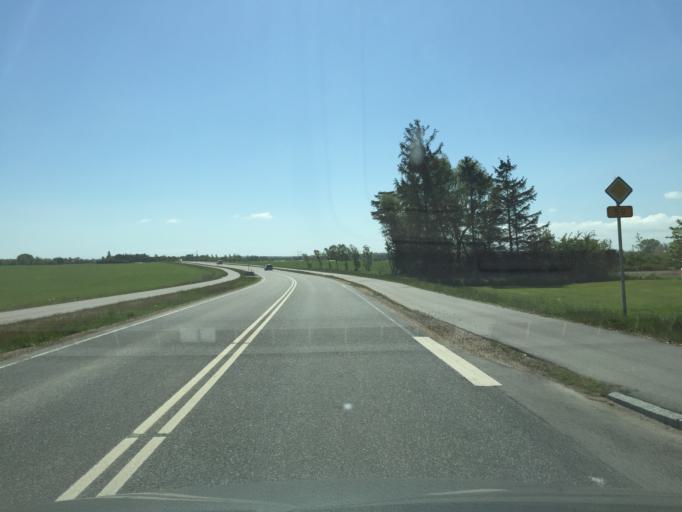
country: DK
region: Zealand
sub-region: Vordingborg Kommune
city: Stege
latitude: 54.9747
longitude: 12.1943
